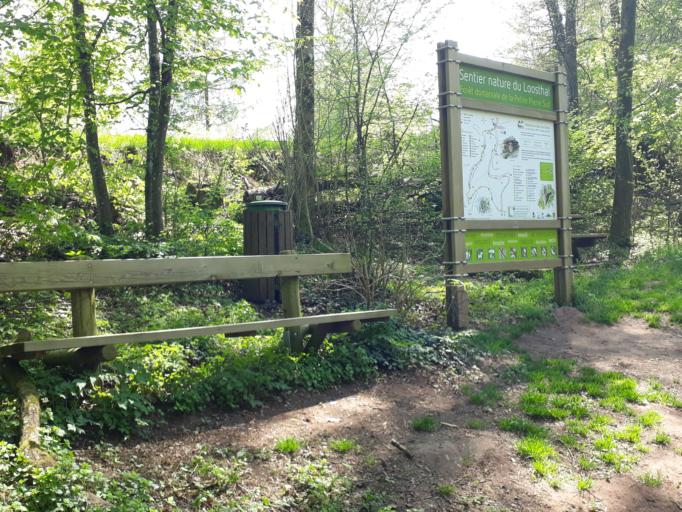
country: FR
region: Alsace
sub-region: Departement du Bas-Rhin
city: Neuwiller-les-Saverne
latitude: 48.8506
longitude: 7.3419
